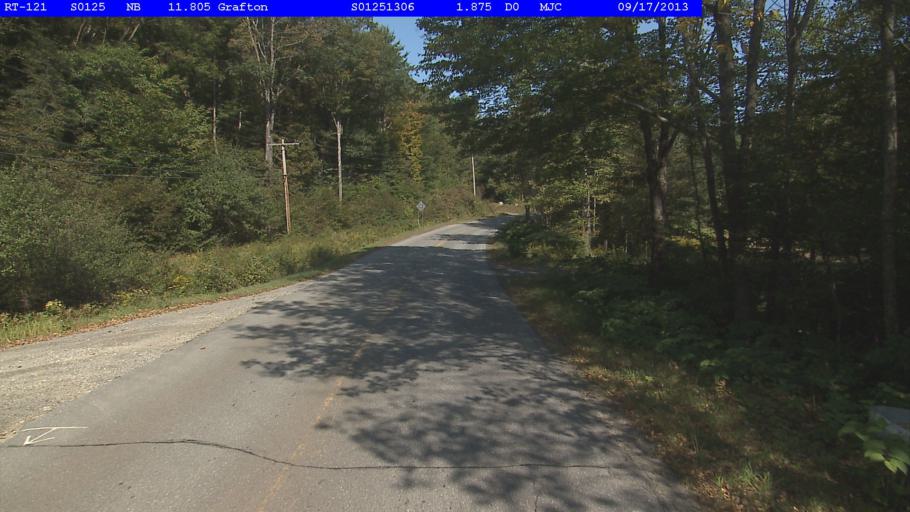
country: US
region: Vermont
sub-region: Windham County
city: Rockingham
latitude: 43.1661
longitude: -72.5769
